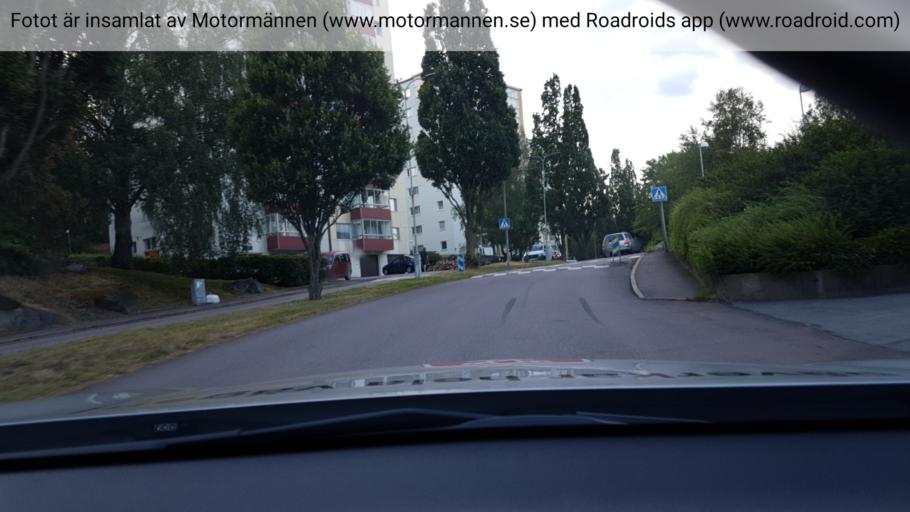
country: SE
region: Vaestra Goetaland
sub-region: Goteborg
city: Majorna
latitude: 57.7132
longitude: 11.8909
